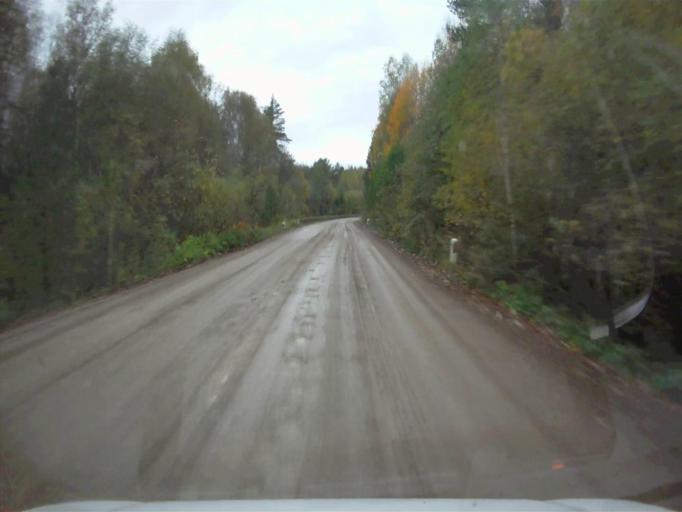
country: RU
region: Chelyabinsk
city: Nyazepetrovsk
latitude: 56.1277
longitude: 59.3321
